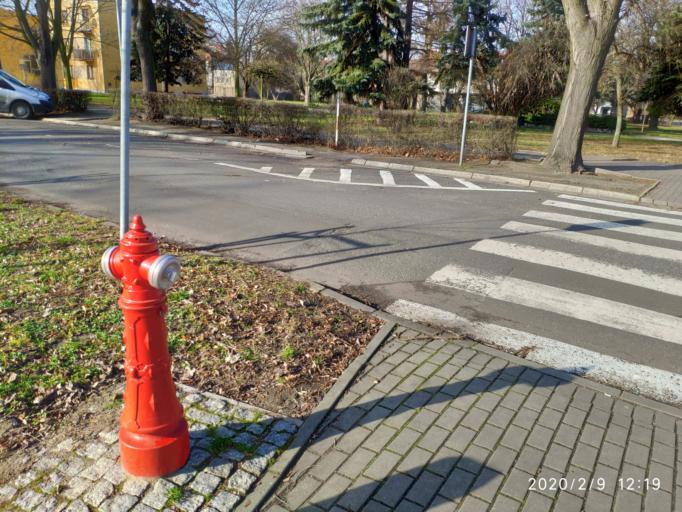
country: PL
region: Lower Silesian Voivodeship
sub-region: Powiat glogowski
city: Glogow
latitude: 51.6633
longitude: 16.0839
